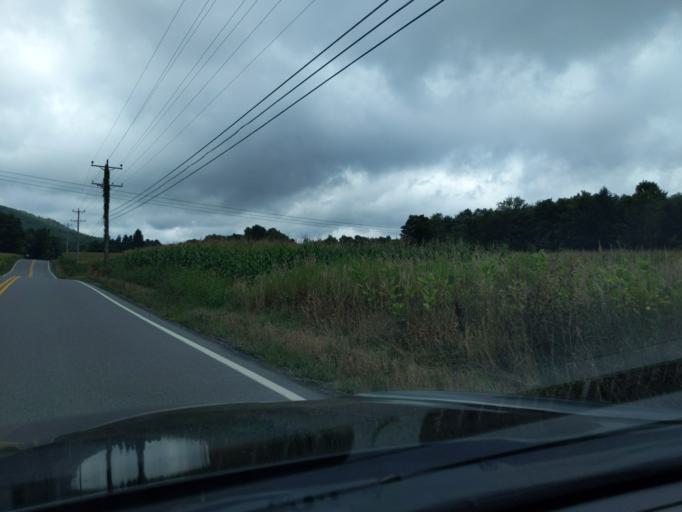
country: US
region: Pennsylvania
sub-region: Blair County
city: Claysburg
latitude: 40.3375
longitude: -78.5593
